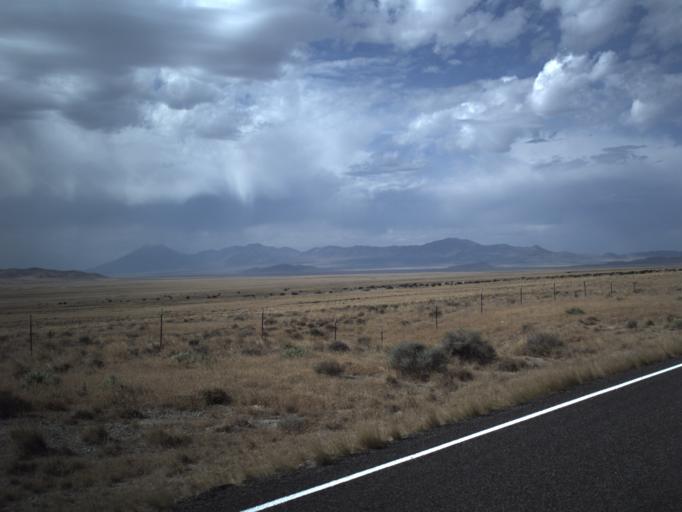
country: US
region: Utah
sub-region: Tooele County
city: Wendover
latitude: 41.4393
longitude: -113.7195
